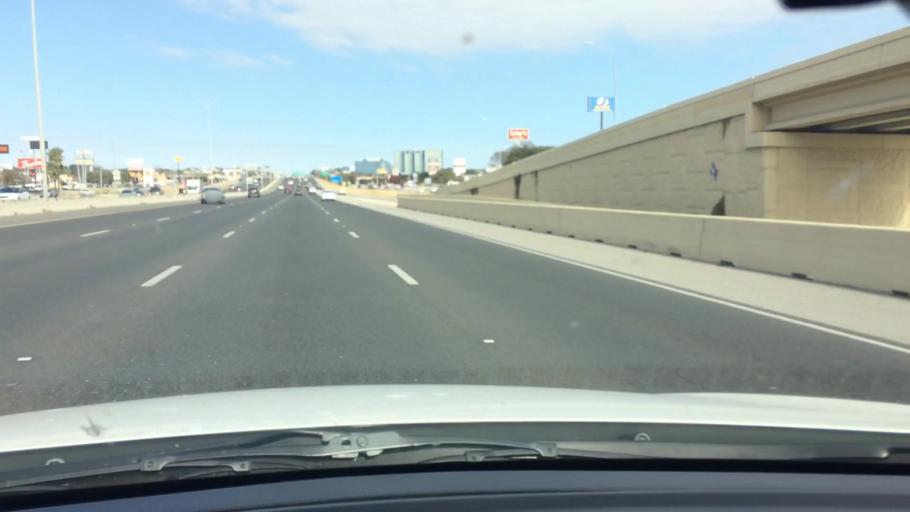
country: US
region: Texas
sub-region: Bexar County
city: Hollywood Park
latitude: 29.5590
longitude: -98.4834
